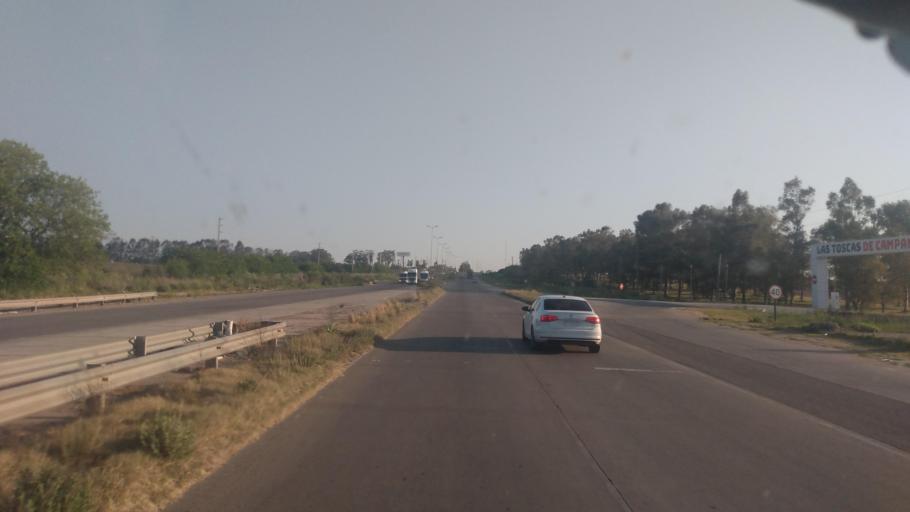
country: AR
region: Buenos Aires
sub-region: Partido de Campana
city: Campana
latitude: -34.2125
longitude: -58.9585
